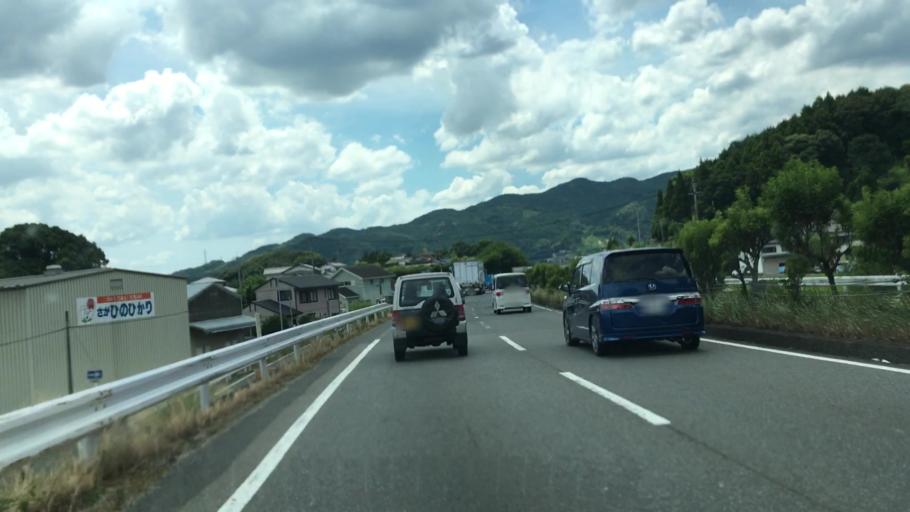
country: JP
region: Saga Prefecture
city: Tosu
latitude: 33.4262
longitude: 130.5171
